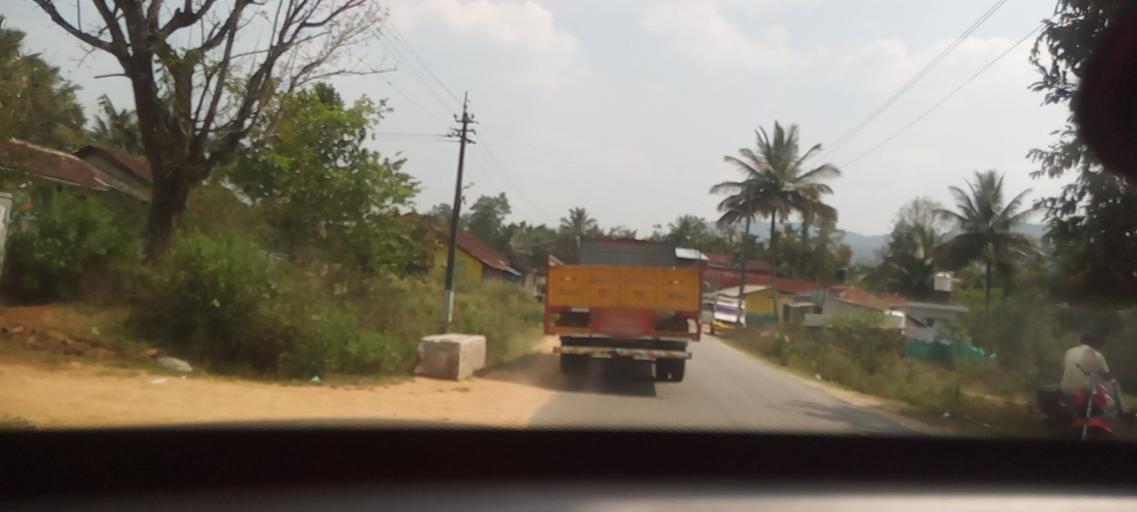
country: IN
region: Karnataka
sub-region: Chikmagalur
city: Mudigere
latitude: 13.3055
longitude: 75.5853
